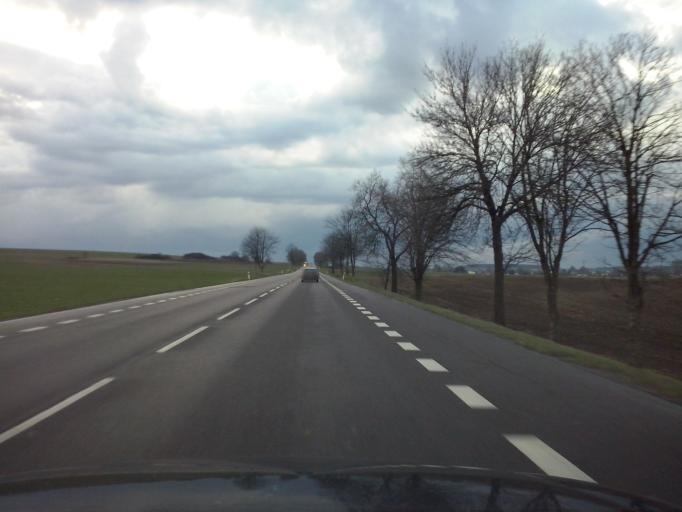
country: PL
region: Lublin Voivodeship
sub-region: Chelm
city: Chelm
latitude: 51.1662
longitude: 23.3714
